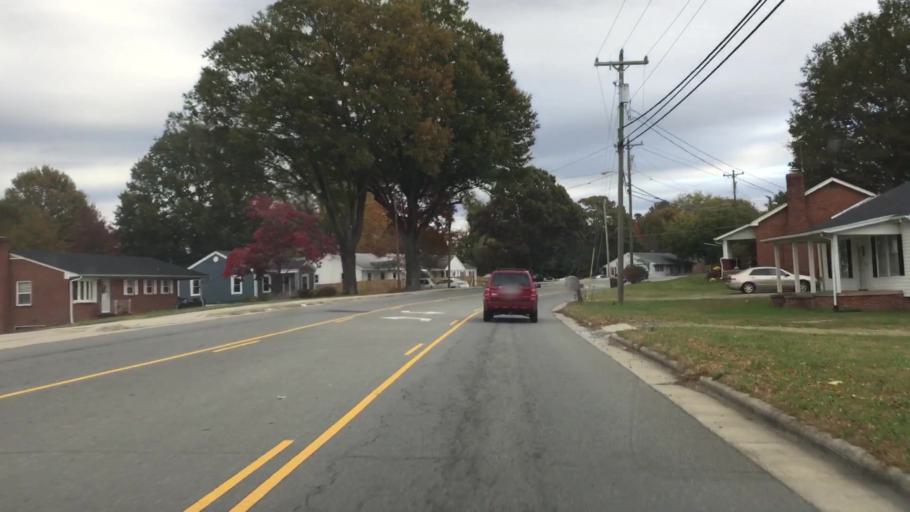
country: US
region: North Carolina
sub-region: Rockingham County
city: Reidsville
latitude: 36.3536
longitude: -79.6867
